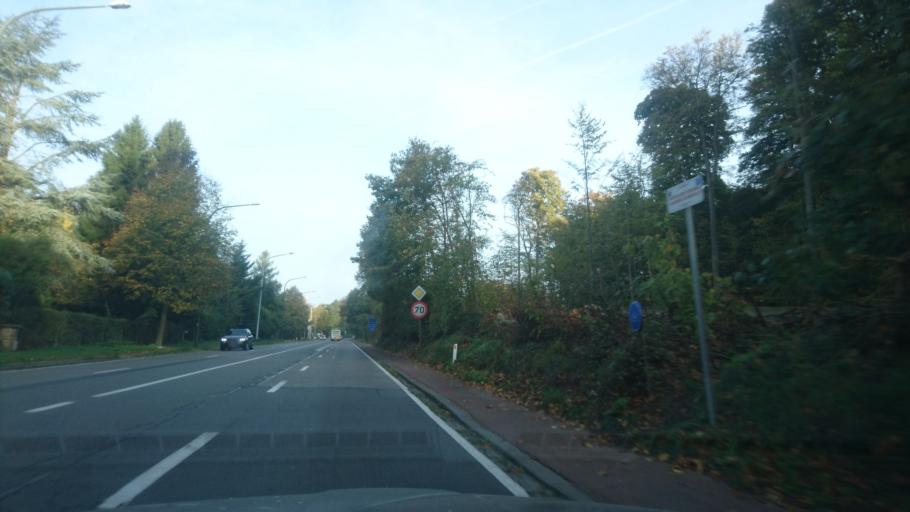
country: BE
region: Flanders
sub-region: Provincie Vlaams-Brabant
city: Sint-Genesius-Rode
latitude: 50.7569
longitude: 4.3869
